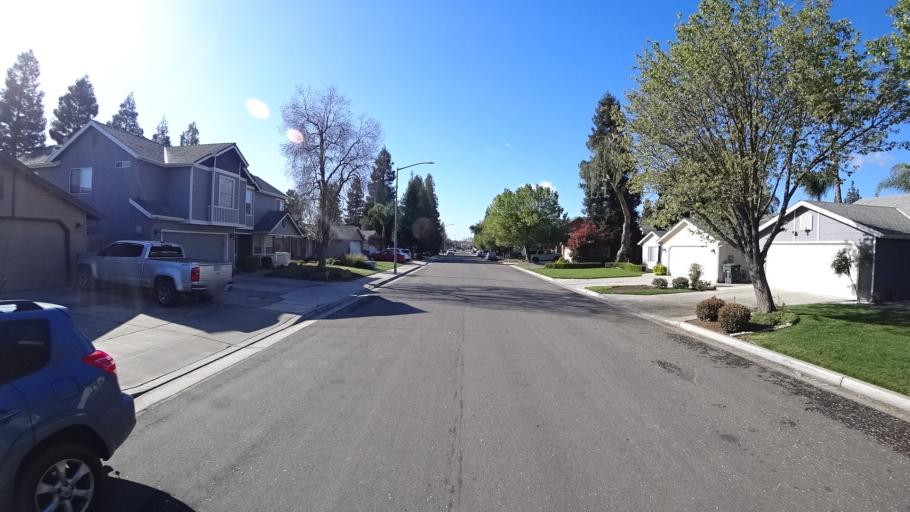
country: US
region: California
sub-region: Fresno County
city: West Park
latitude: 36.8244
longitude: -119.8727
